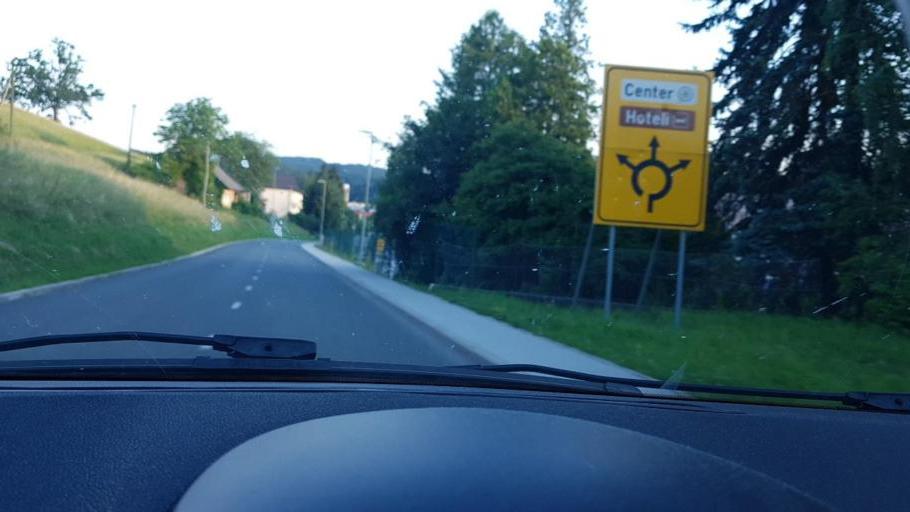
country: SI
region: Rogaska Slatina
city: Rogaska Slatina
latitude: 46.2468
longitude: 15.6268
